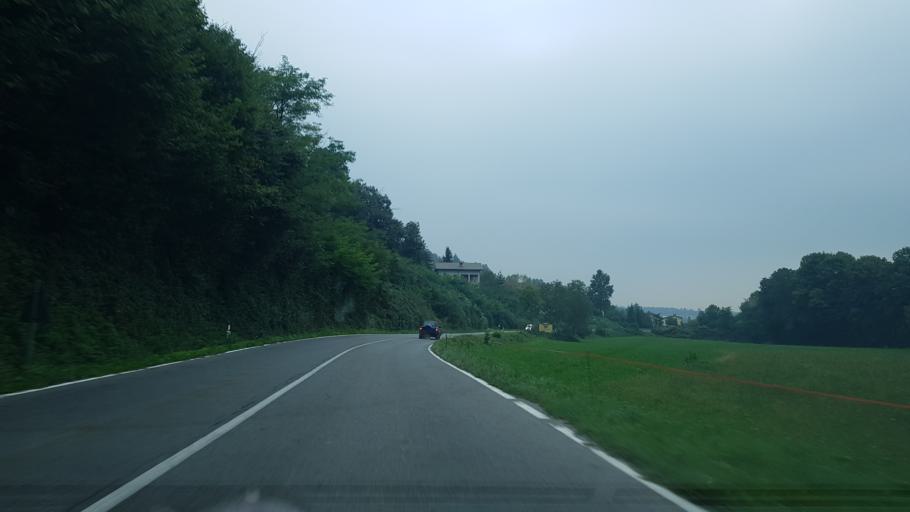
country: IT
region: Piedmont
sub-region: Provincia di Cuneo
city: Frabosa Sottana
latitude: 44.3288
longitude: 7.7886
